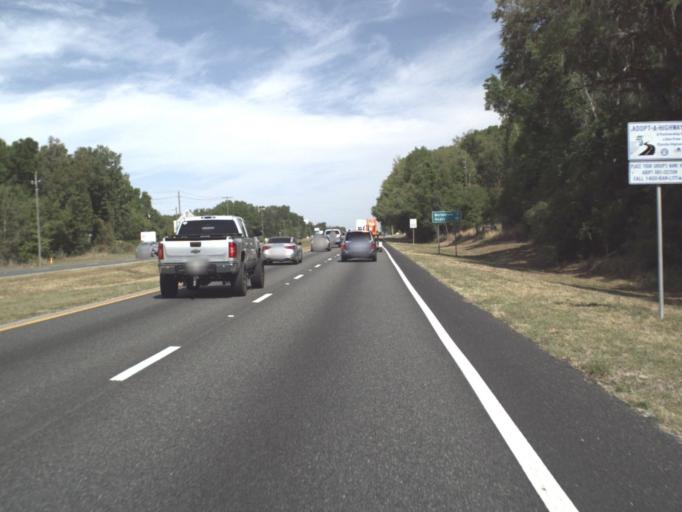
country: US
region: Florida
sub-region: Sumter County
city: The Villages
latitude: 28.9835
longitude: -81.9883
